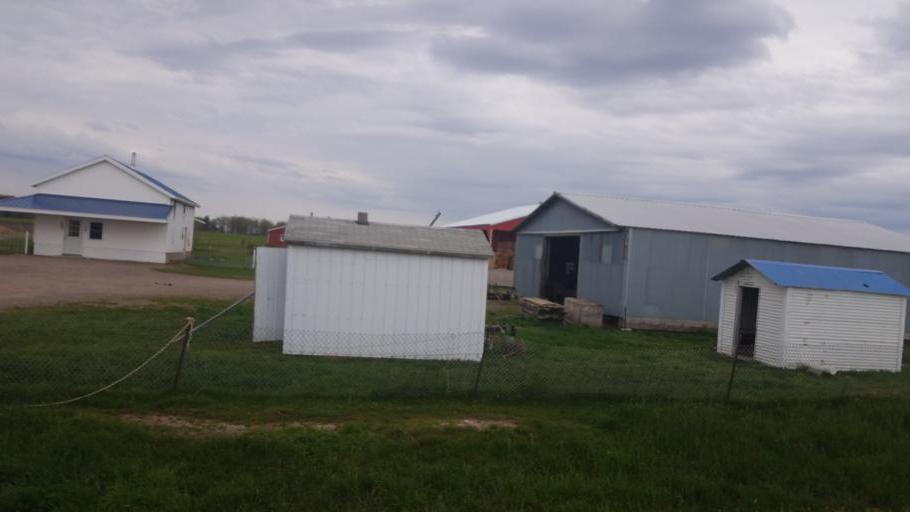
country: US
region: Wisconsin
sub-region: Marathon County
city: Spencer
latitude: 44.6498
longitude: -90.3772
